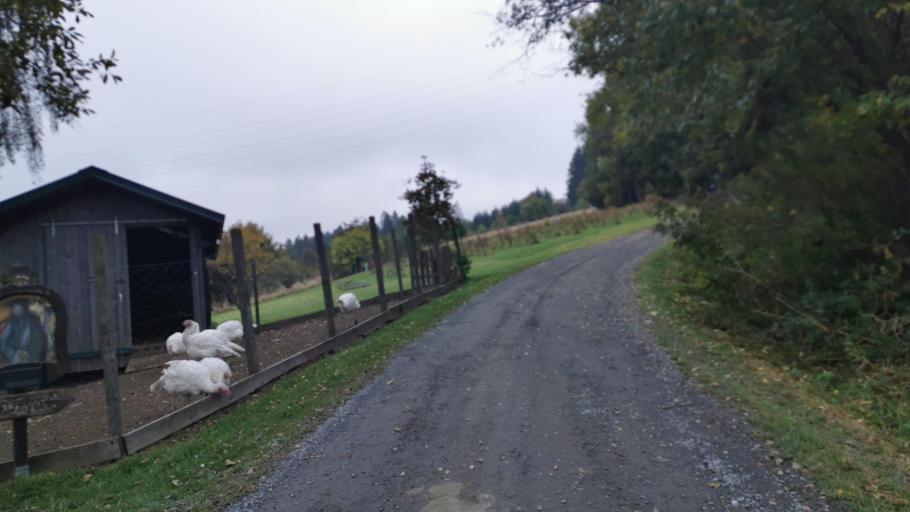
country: DE
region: Bavaria
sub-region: Upper Franconia
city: Teuschnitz
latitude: 50.4322
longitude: 11.3423
